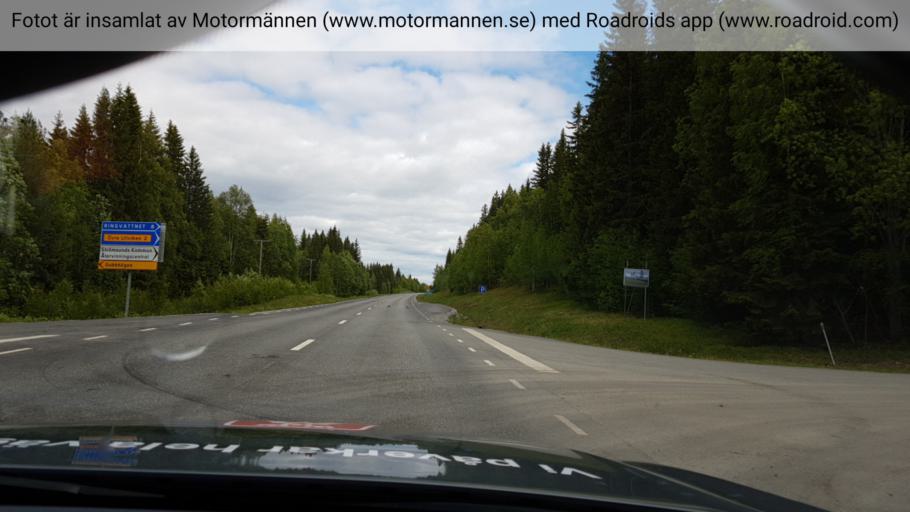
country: SE
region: Jaemtland
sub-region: Stroemsunds Kommun
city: Stroemsund
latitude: 64.2221
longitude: 15.5330
